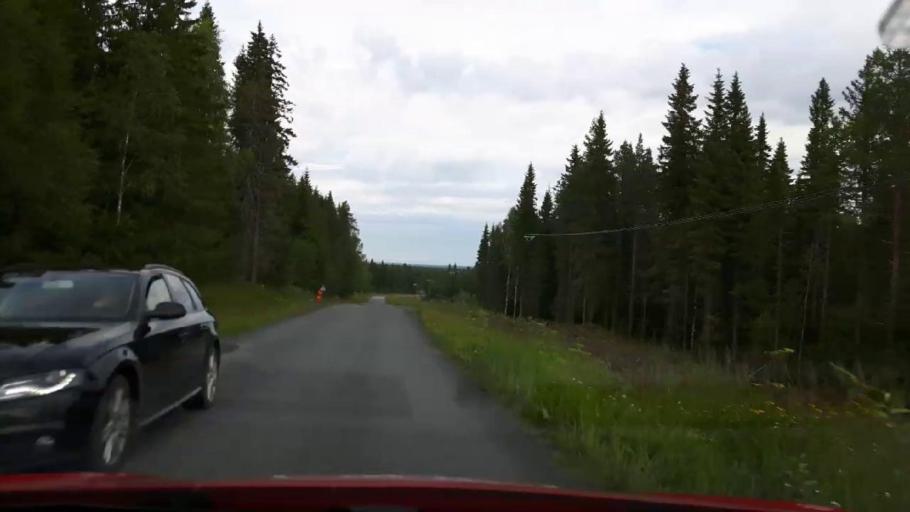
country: SE
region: Jaemtland
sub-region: Stroemsunds Kommun
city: Stroemsund
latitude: 63.5291
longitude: 15.3583
